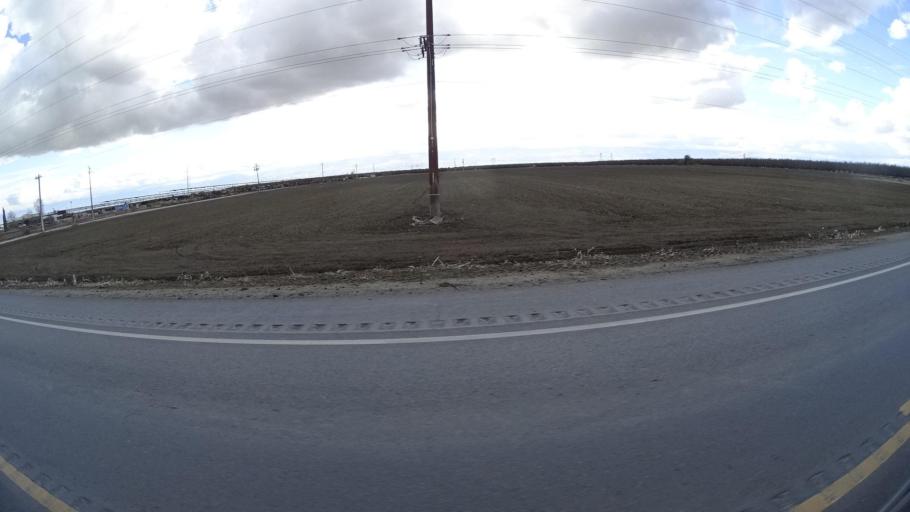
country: US
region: California
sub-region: Kern County
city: Greenfield
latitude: 35.2089
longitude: -119.0976
